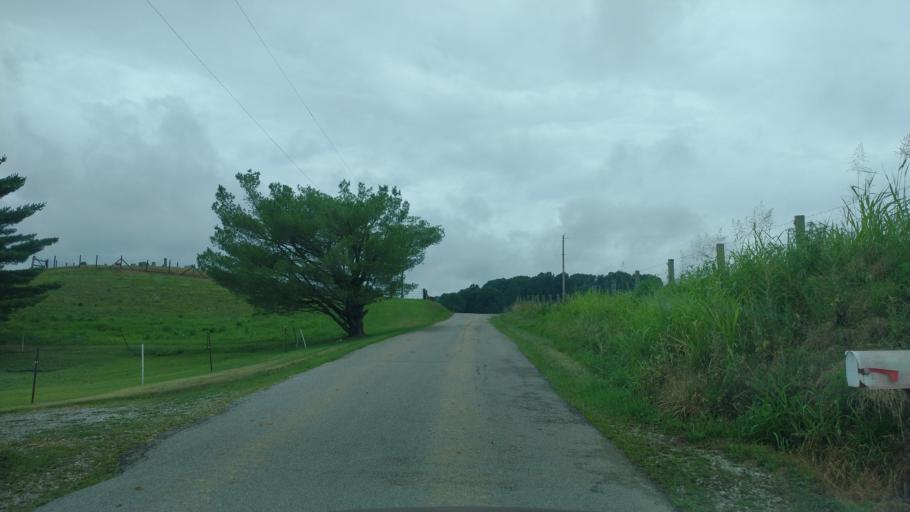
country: US
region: West Virginia
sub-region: Mason County
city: New Haven
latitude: 38.9247
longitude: -81.9741
